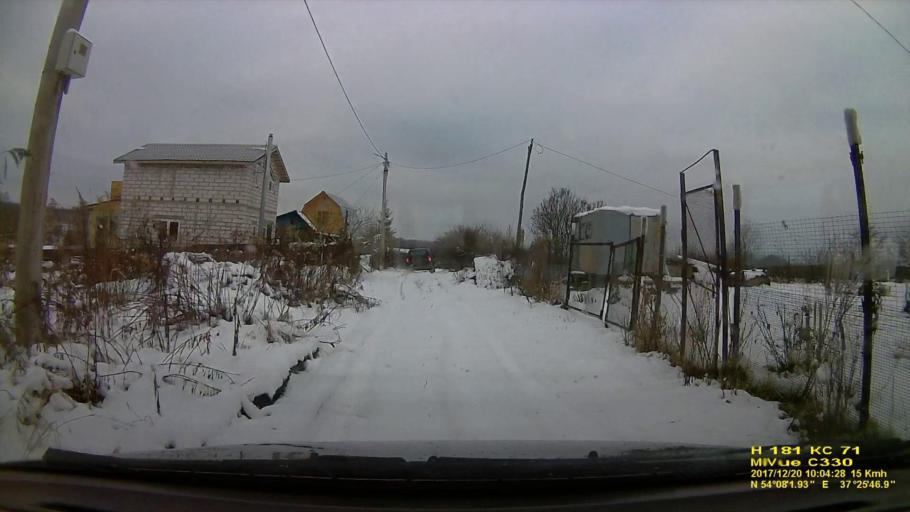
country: RU
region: Tula
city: Kosaya Gora
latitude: 54.1339
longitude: 37.4296
